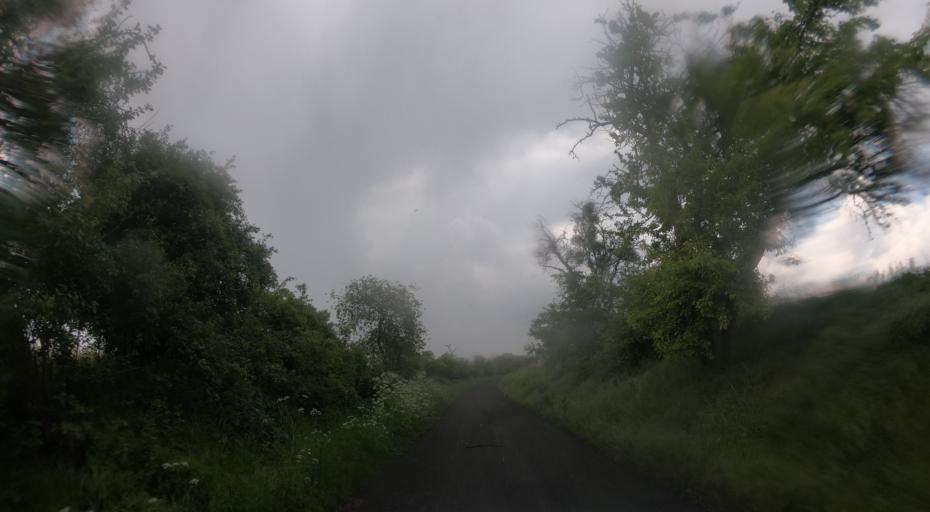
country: PL
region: West Pomeranian Voivodeship
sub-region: Powiat pyrzycki
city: Bielice
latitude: 53.2619
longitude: 14.6996
